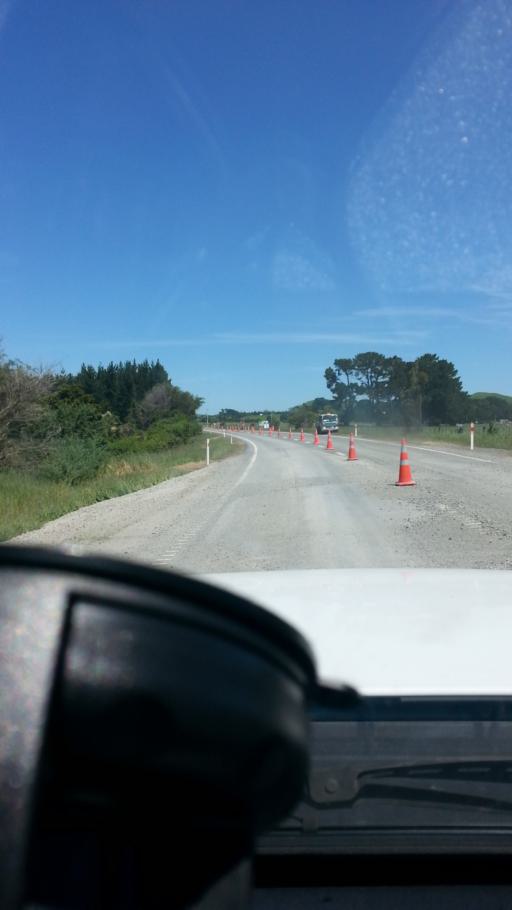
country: NZ
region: Wellington
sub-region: Masterton District
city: Masterton
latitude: -40.7845
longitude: 175.6164
